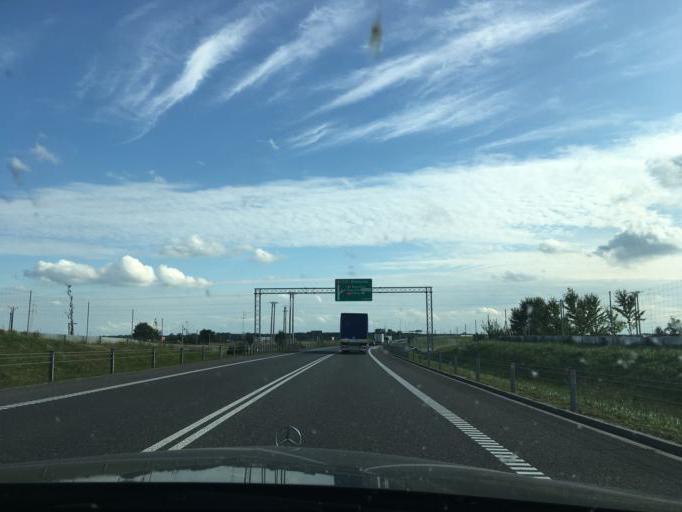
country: PL
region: Podlasie
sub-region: Powiat augustowski
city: Augustow
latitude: 53.8392
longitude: 22.9543
